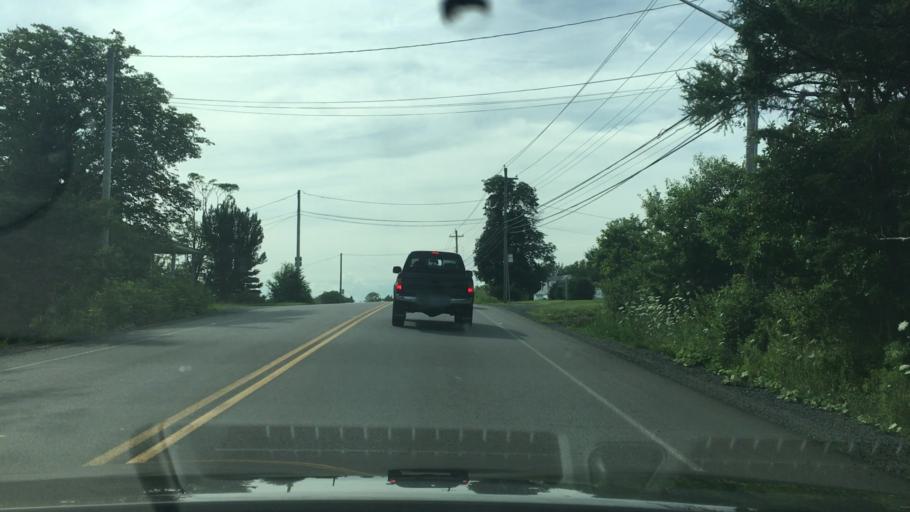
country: CA
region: Nova Scotia
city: Dartmouth
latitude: 44.7305
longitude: -63.7535
